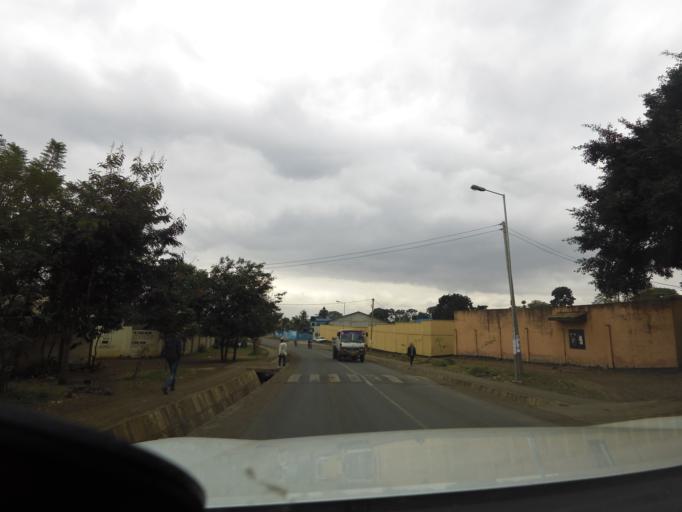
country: TZ
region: Arusha
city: Arusha
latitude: -3.3637
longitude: 36.6608
